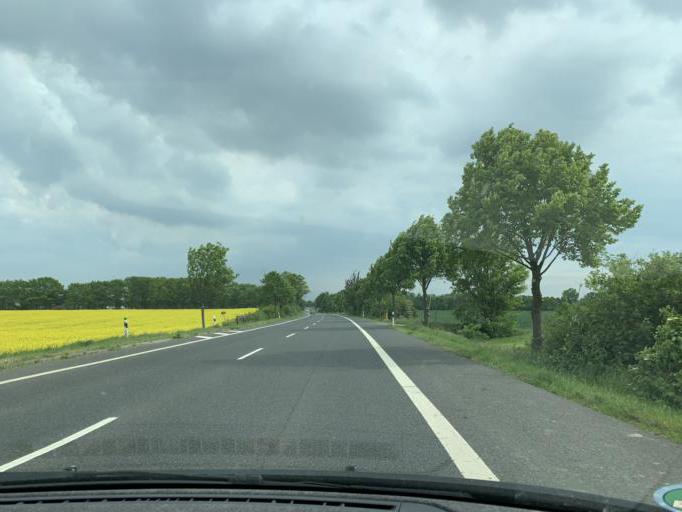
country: DE
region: North Rhine-Westphalia
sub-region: Regierungsbezirk Koln
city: Norvenich
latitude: 50.7672
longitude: 6.6334
